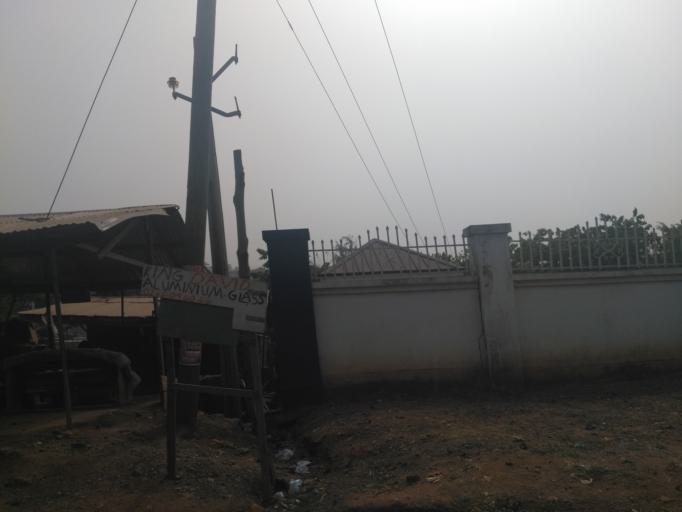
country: GH
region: Ashanti
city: Kumasi
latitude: 6.7121
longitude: -1.6405
